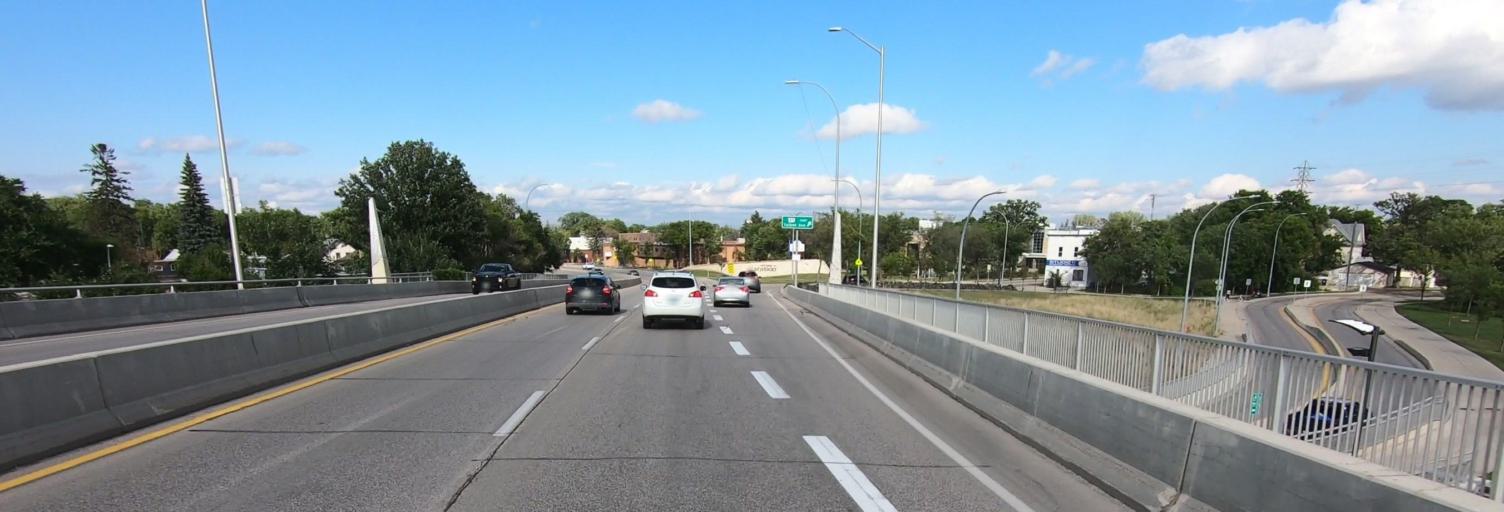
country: CA
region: Manitoba
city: Winnipeg
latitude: 49.9092
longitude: -97.1198
